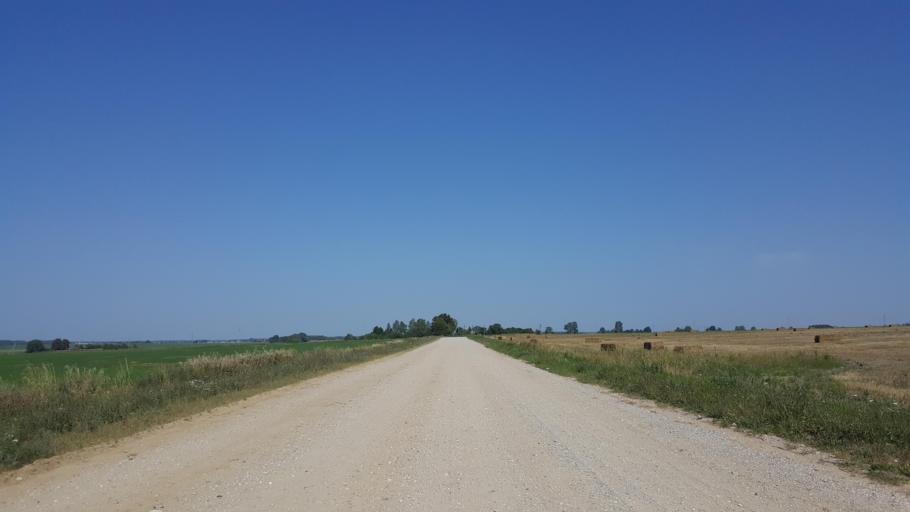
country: PL
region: Podlasie
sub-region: Powiat hajnowski
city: Czeremcha
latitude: 52.4568
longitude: 23.4467
